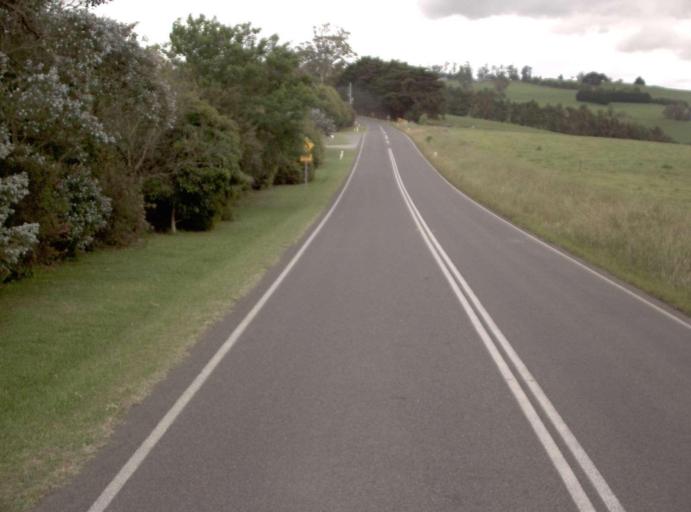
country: AU
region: Victoria
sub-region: Baw Baw
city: Warragul
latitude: -38.1138
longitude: 145.9774
